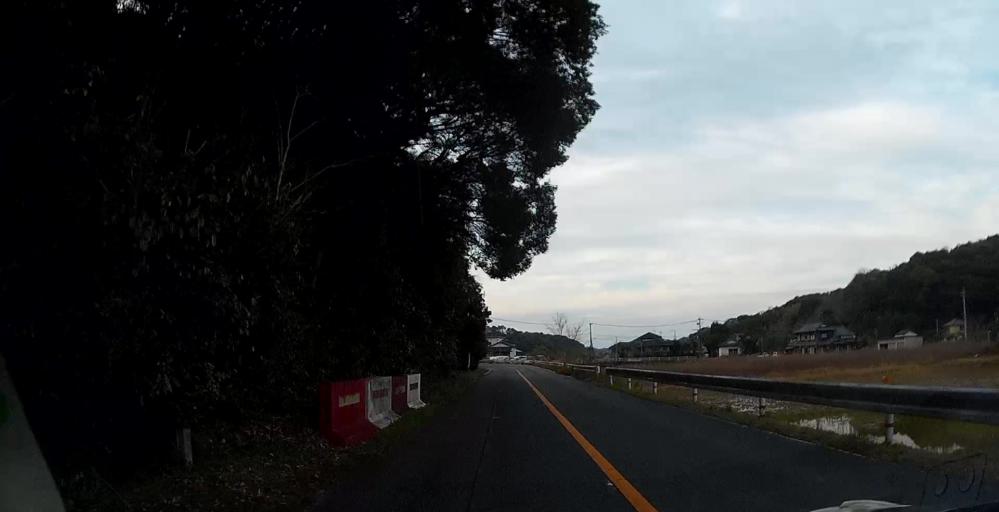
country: JP
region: Kumamoto
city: Hondo
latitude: 32.5077
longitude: 130.3829
